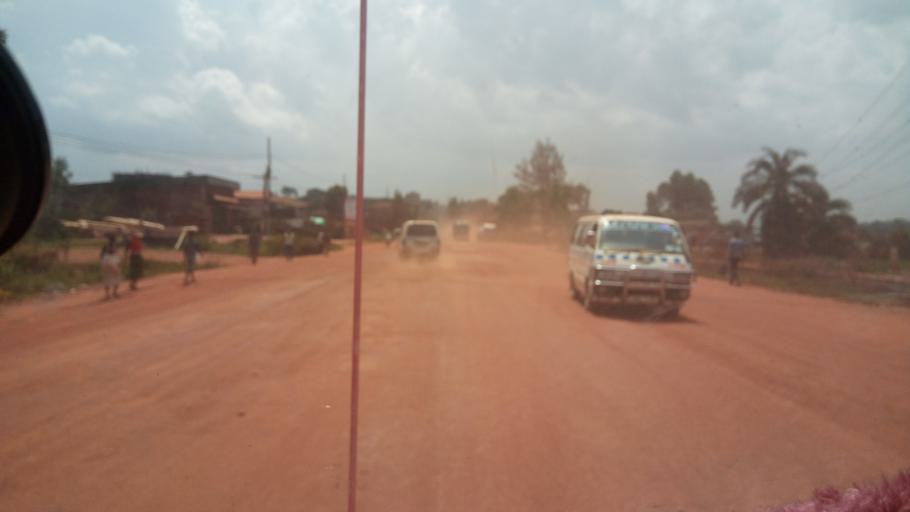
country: UG
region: Central Region
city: Kampala Central Division
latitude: 0.3478
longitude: 32.5406
